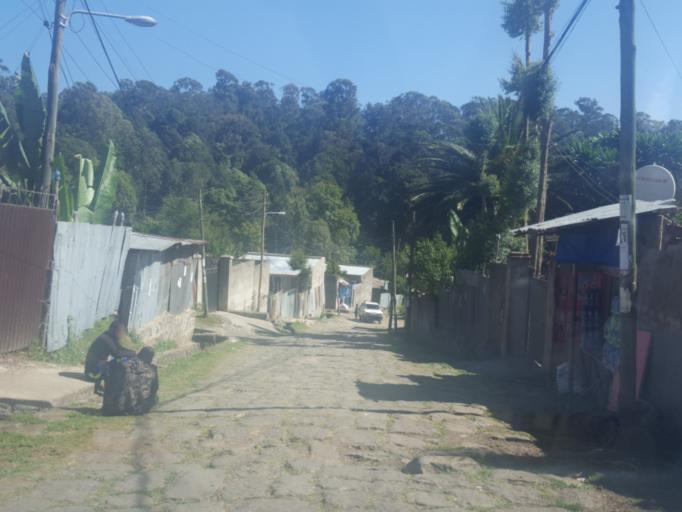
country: ET
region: Adis Abeba
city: Addis Ababa
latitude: 9.0499
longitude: 38.7678
